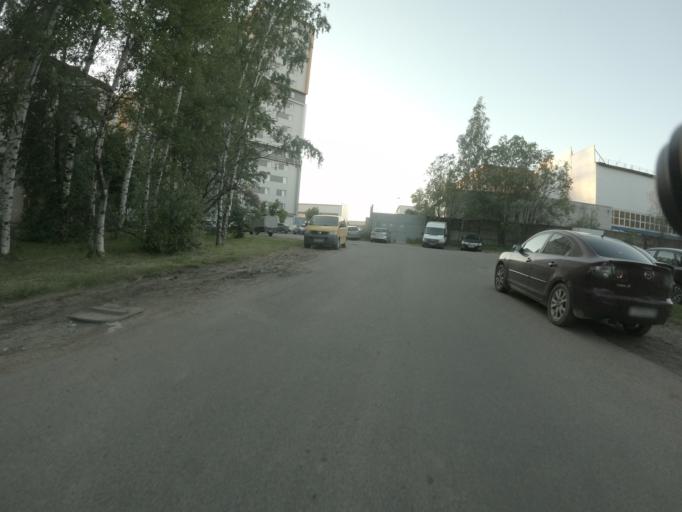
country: RU
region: St.-Petersburg
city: Krasnogvargeisky
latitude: 59.9784
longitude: 30.5146
